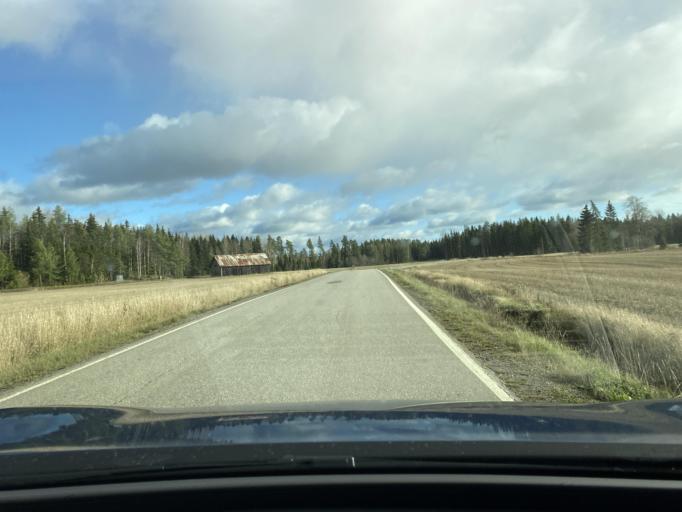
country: FI
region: Varsinais-Suomi
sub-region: Loimaa
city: Aura
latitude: 60.7022
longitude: 22.6233
